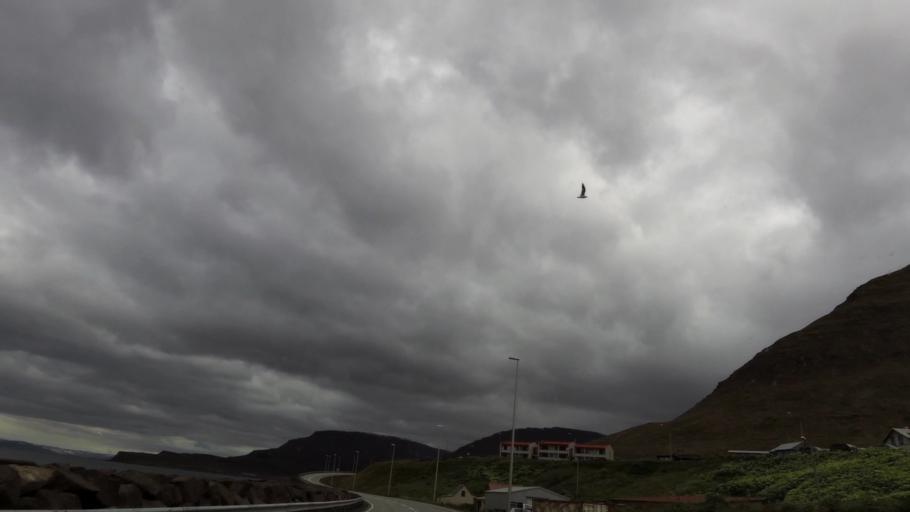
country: IS
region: Westfjords
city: Isafjoerdur
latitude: 66.1099
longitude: -23.1184
